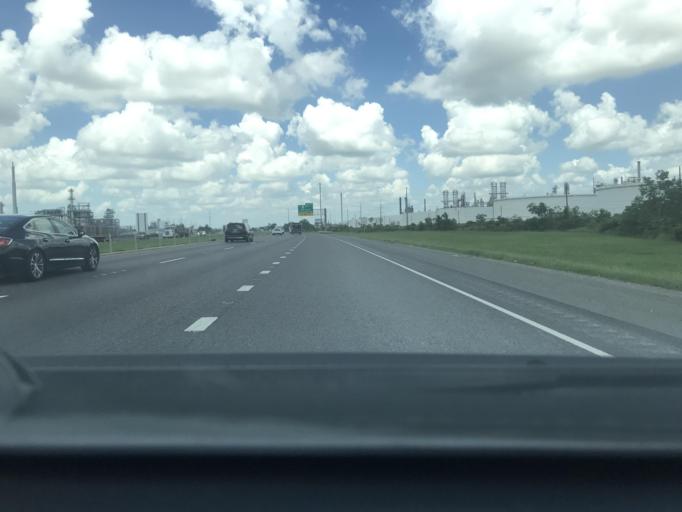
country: US
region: Louisiana
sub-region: Calcasieu Parish
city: Westlake
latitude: 30.2374
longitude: -93.2654
